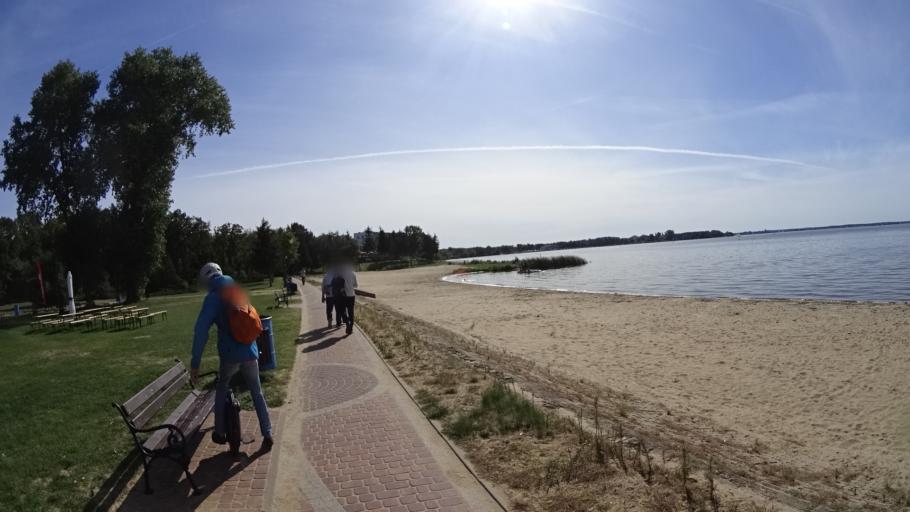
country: PL
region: Masovian Voivodeship
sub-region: Powiat legionowski
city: Bialobrzegi
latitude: 52.4603
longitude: 21.0687
